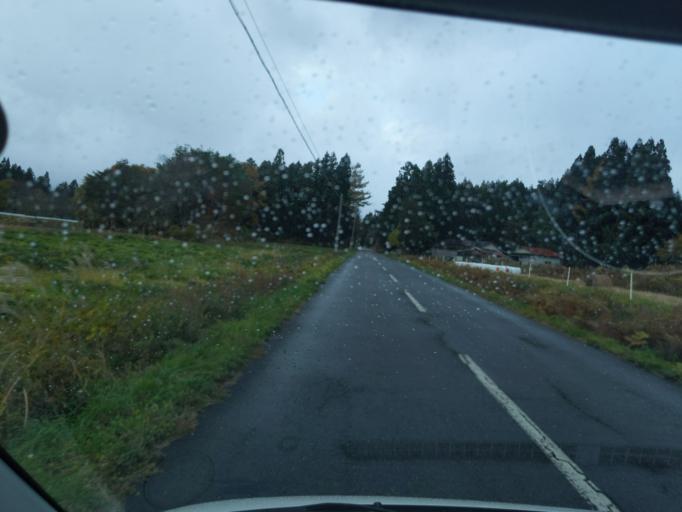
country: JP
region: Iwate
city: Mizusawa
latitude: 39.0924
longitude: 140.9947
